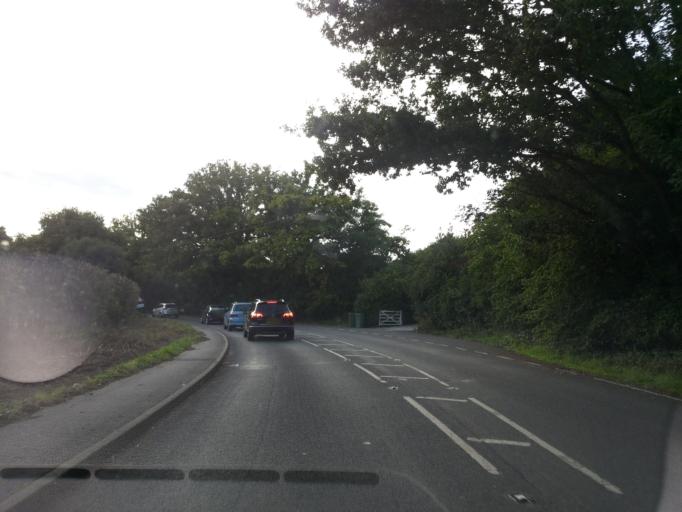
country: GB
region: England
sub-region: Surrey
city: Windlesham
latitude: 51.3652
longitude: -0.6715
